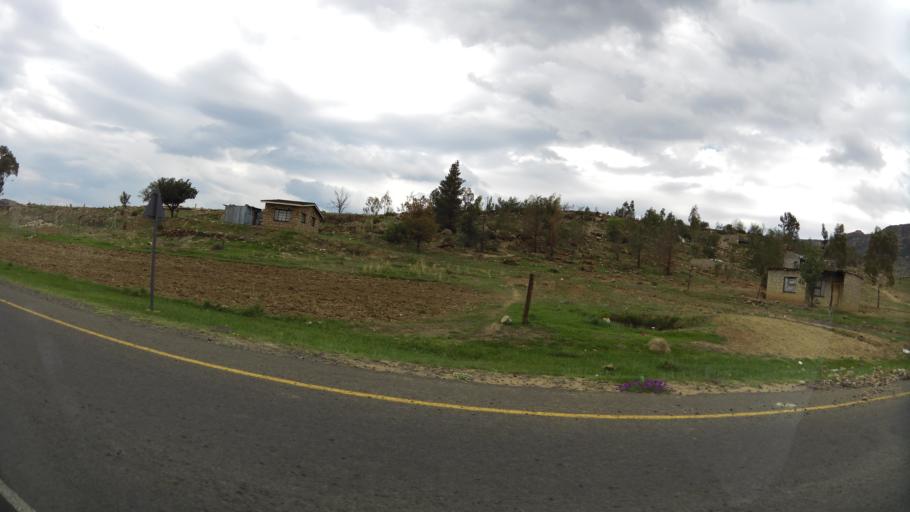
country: LS
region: Maseru
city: Maseru
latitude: -29.4030
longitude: 27.4732
